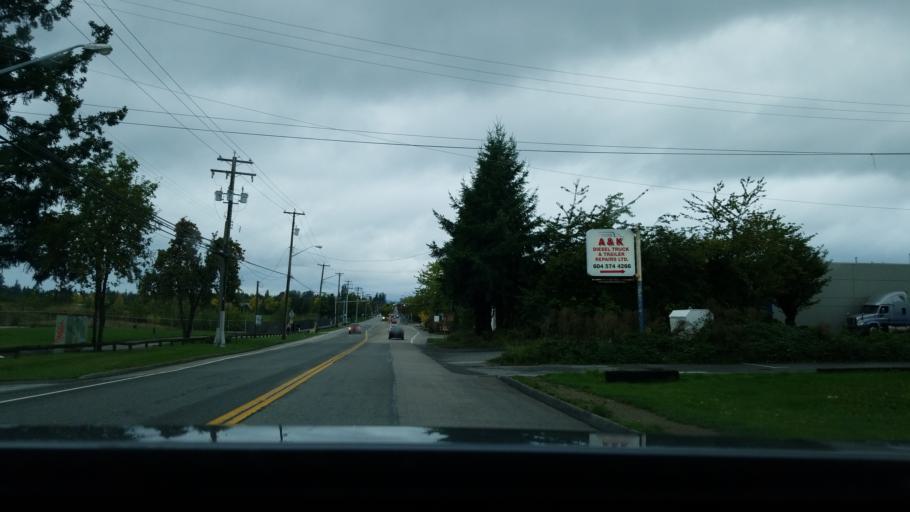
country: CA
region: British Columbia
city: Langley
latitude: 49.1188
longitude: -122.7276
